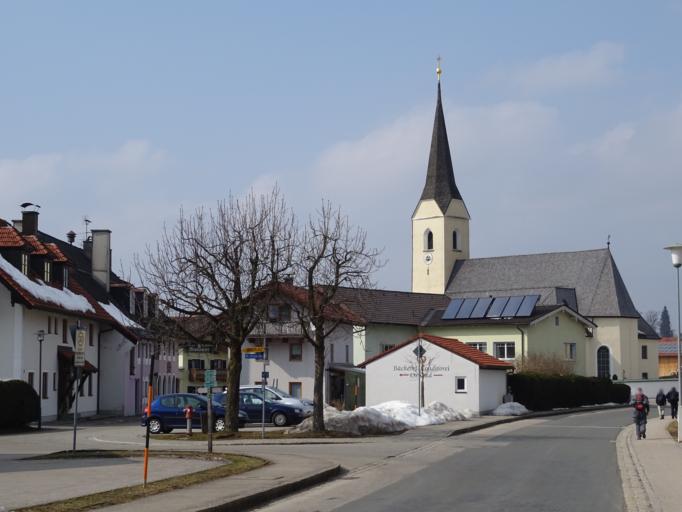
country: DE
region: Bavaria
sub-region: Upper Bavaria
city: Surberg
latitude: 47.8327
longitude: 12.7437
